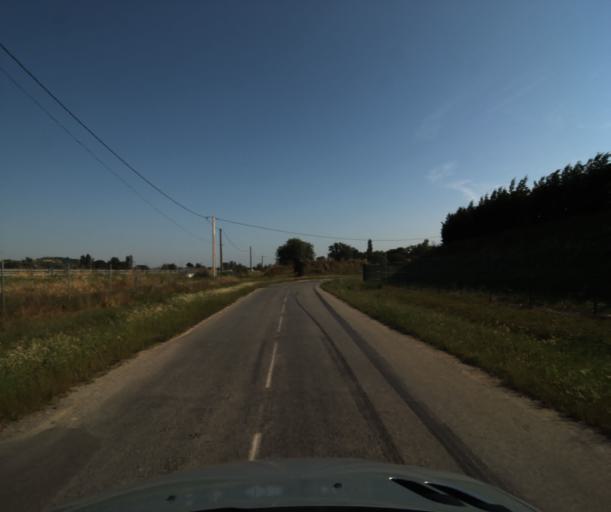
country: FR
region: Midi-Pyrenees
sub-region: Departement de la Haute-Garonne
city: Lacroix-Falgarde
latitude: 43.4782
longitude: 1.4063
